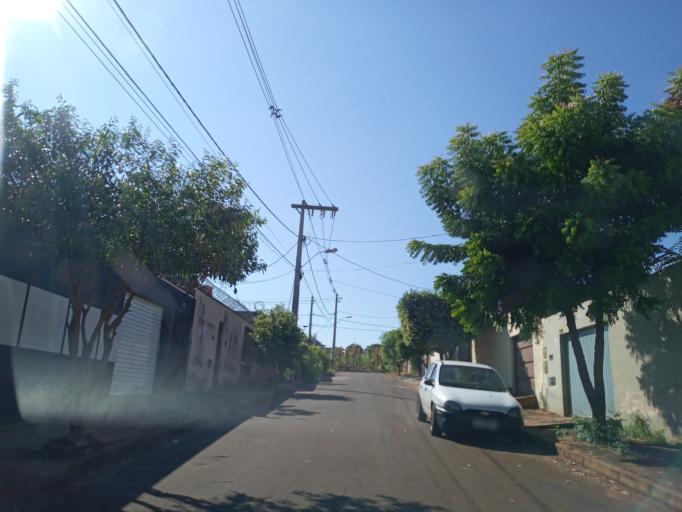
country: BR
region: Minas Gerais
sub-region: Ituiutaba
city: Ituiutaba
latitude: -18.9757
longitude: -49.4904
